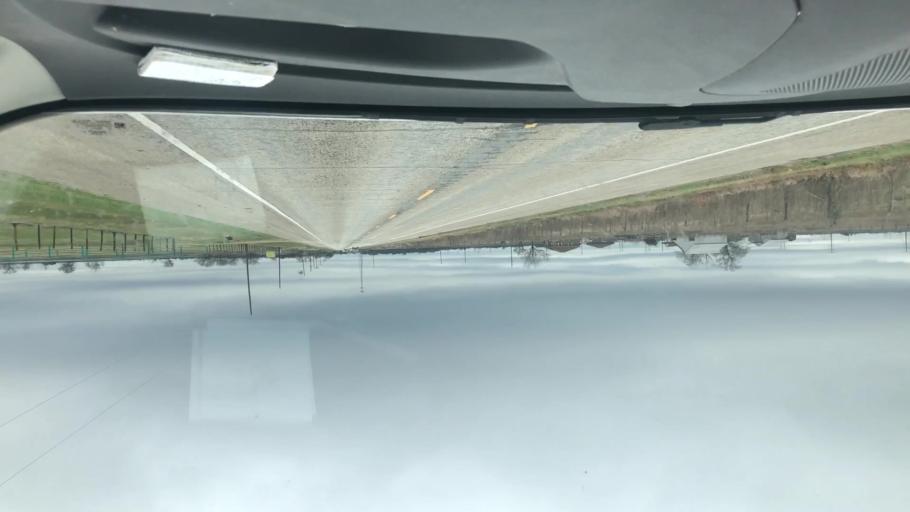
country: US
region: Texas
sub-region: Wharton County
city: Wharton
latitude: 29.2410
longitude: -96.0422
